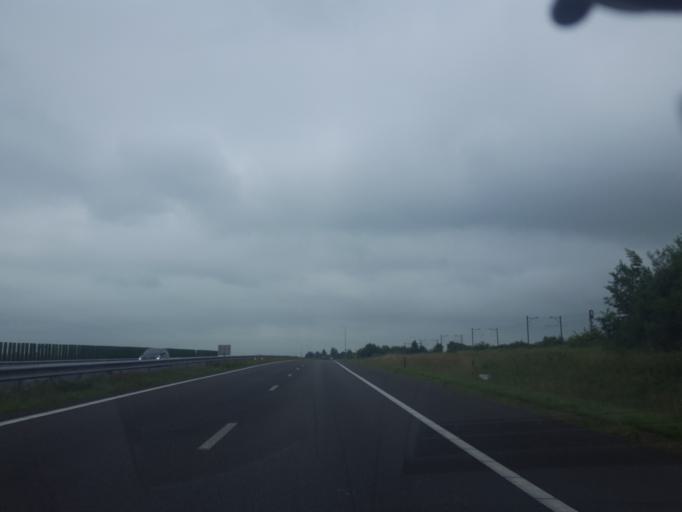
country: NL
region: Friesland
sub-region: Gemeente Boarnsterhim
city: Grou
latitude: 53.0760
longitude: 5.8305
